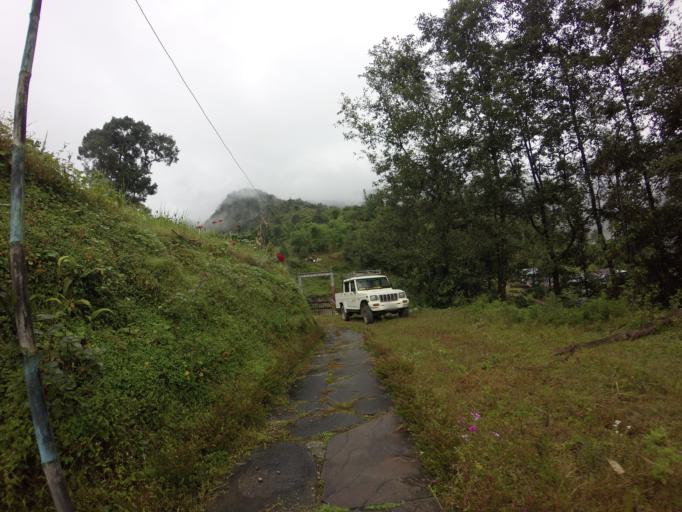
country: NP
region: Western Region
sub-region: Gandaki Zone
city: Pokhara
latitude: 28.3796
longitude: 83.8740
